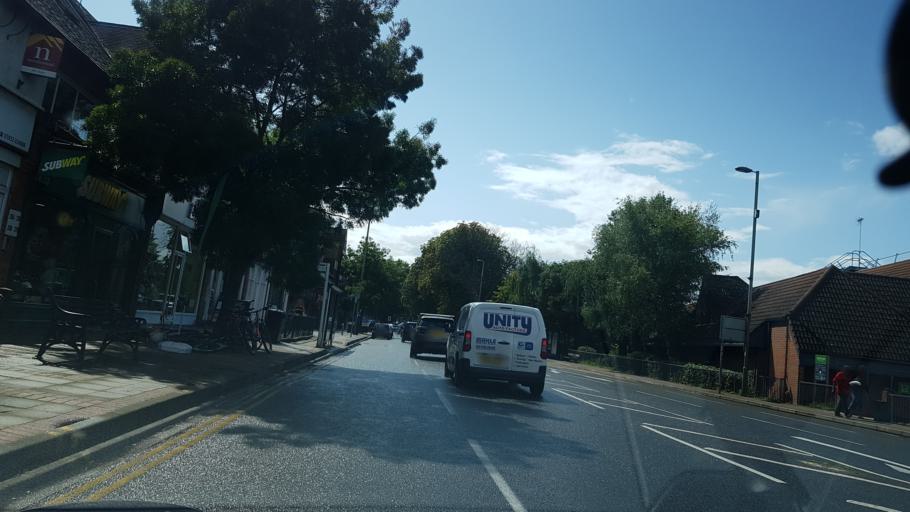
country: GB
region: England
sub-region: Surrey
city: West Byfleet
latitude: 51.3372
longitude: -0.5047
